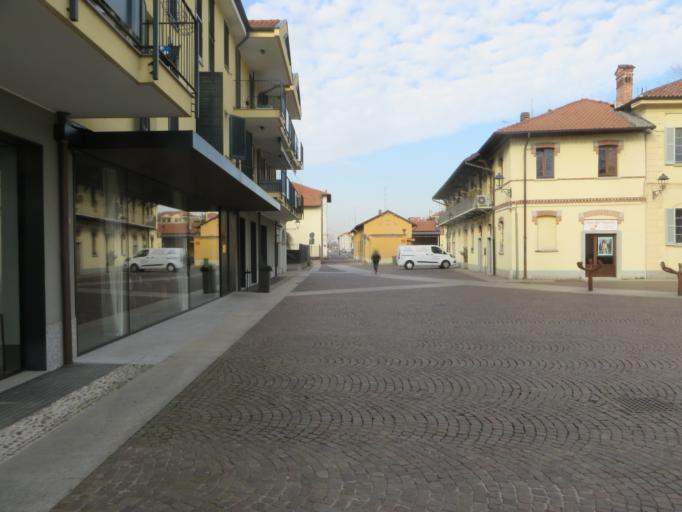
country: IT
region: Lombardy
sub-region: Citta metropolitana di Milano
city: Cornaredo
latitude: 45.4870
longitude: 9.0119
